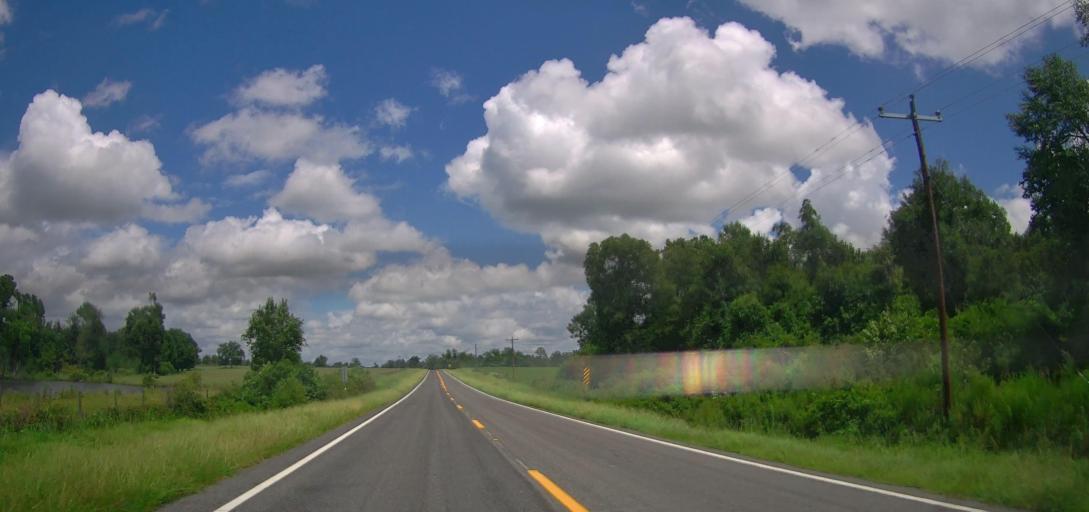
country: US
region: Georgia
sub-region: Turner County
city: Ashburn
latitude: 31.7952
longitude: -83.5845
